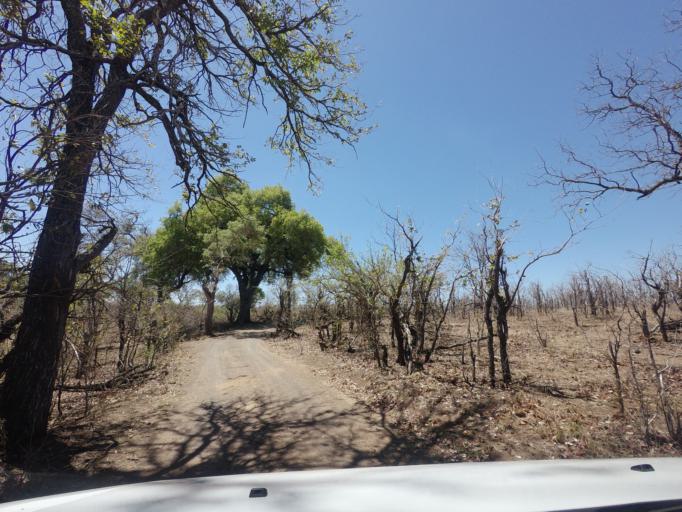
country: ZA
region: Limpopo
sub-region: Mopani District Municipality
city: Phalaborwa
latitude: -23.5402
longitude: 31.4233
